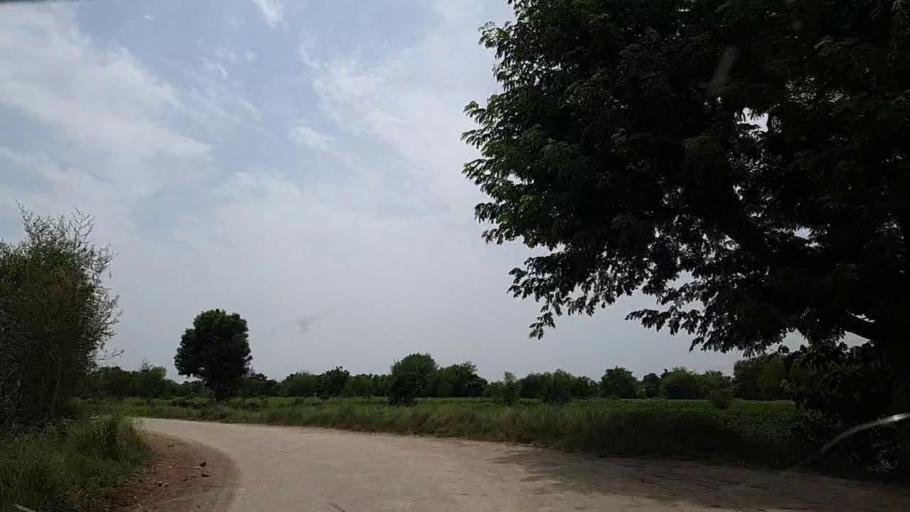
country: PK
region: Sindh
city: Tharu Shah
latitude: 26.9318
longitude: 68.1054
